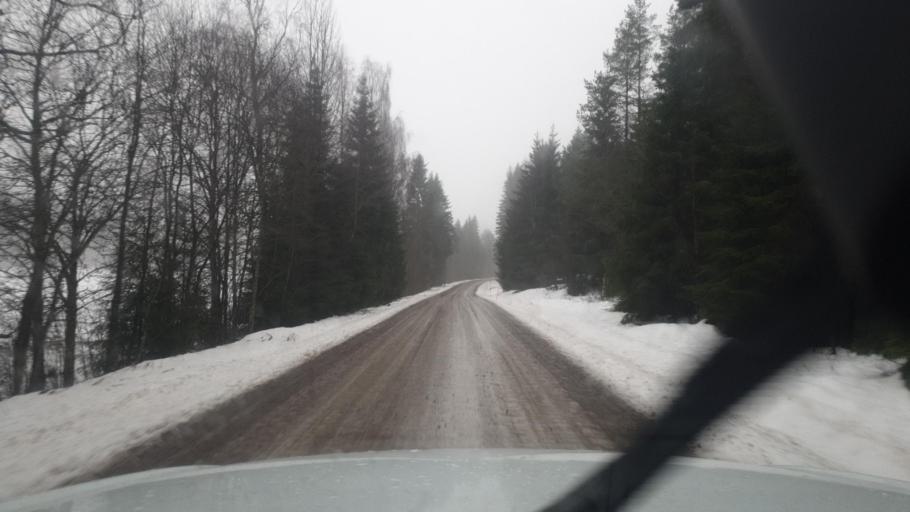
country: SE
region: Vaermland
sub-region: Eda Kommun
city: Charlottenberg
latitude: 60.0843
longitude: 12.5201
